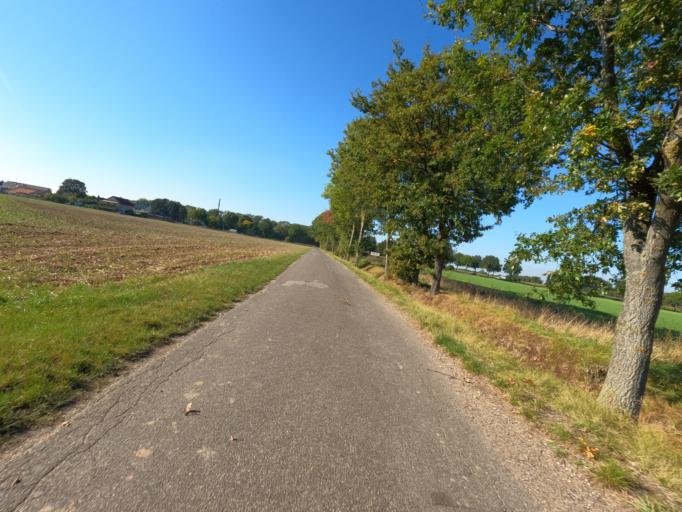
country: DE
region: North Rhine-Westphalia
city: Erkelenz
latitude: 51.0432
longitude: 6.2863
